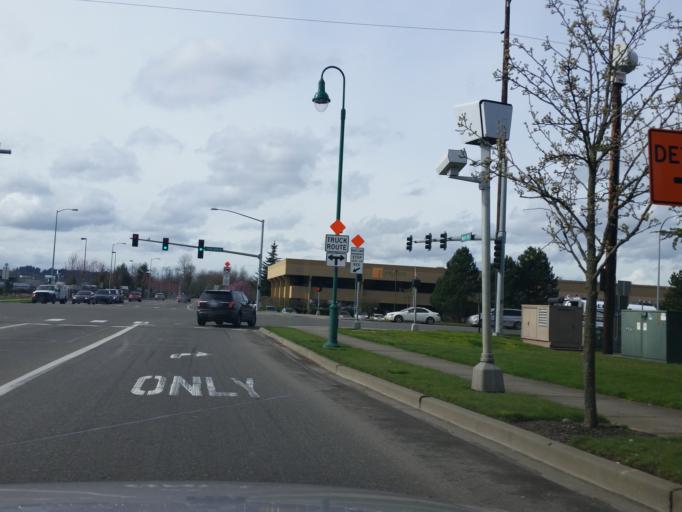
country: US
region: Washington
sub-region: Pierce County
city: Fife
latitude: 47.2280
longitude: -122.3357
